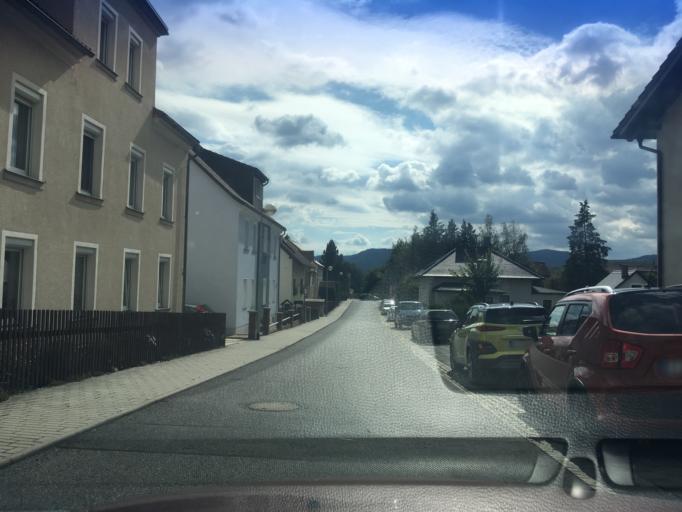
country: DE
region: Saxony
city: Mittelherwigsdorf
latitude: 50.9009
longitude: 14.7750
